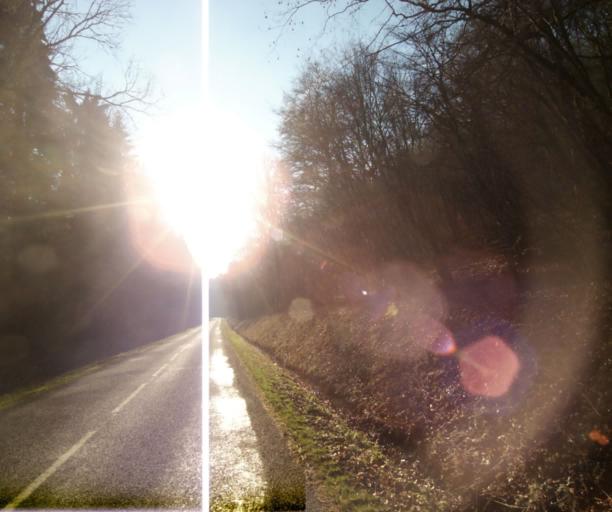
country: FR
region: Champagne-Ardenne
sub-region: Departement de la Haute-Marne
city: Chevillon
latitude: 48.5334
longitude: 5.1839
